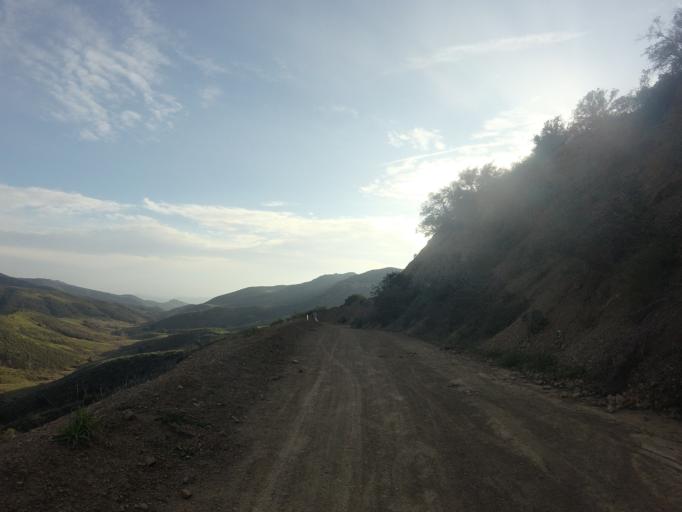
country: US
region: California
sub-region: Riverside County
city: Corona
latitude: 33.8214
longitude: -117.6503
